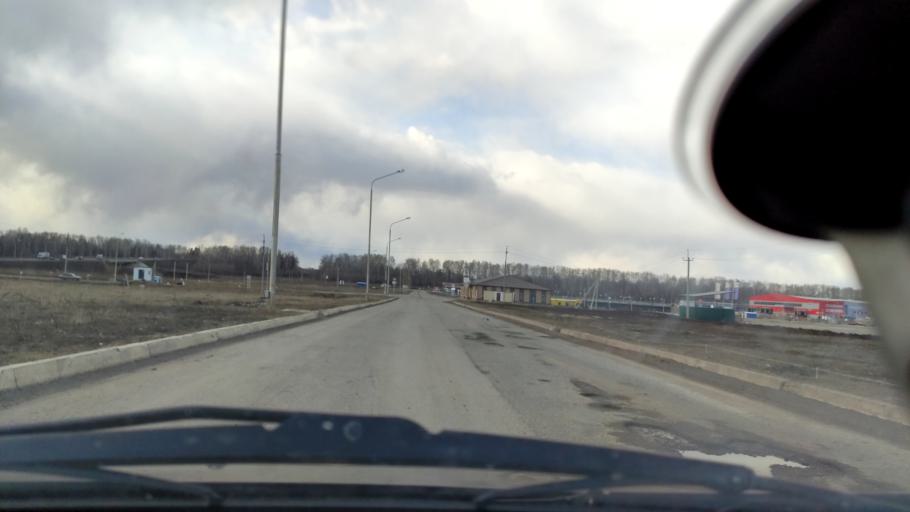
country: RU
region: Bashkortostan
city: Iglino
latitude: 54.7689
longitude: 56.2641
